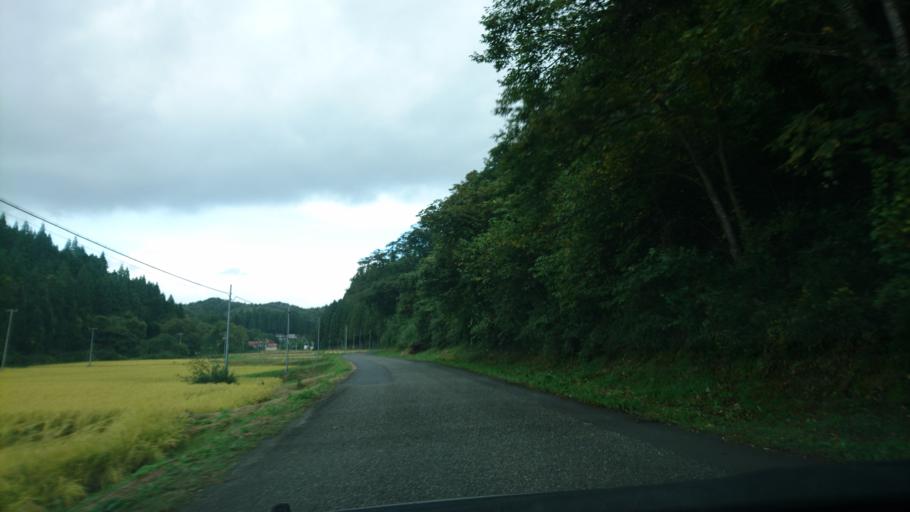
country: JP
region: Iwate
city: Ichinoseki
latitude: 38.8991
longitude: 141.0862
